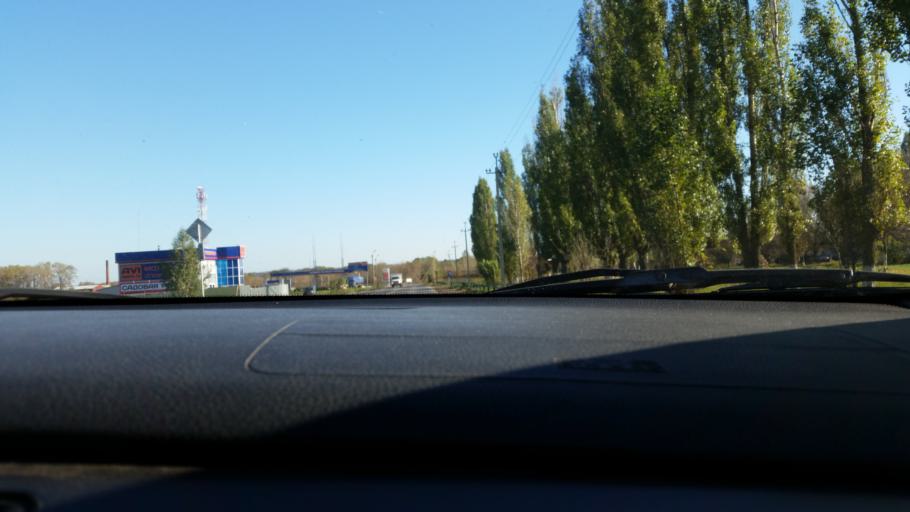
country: RU
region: Lipetsk
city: Gryazi
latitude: 52.4738
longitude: 39.9552
